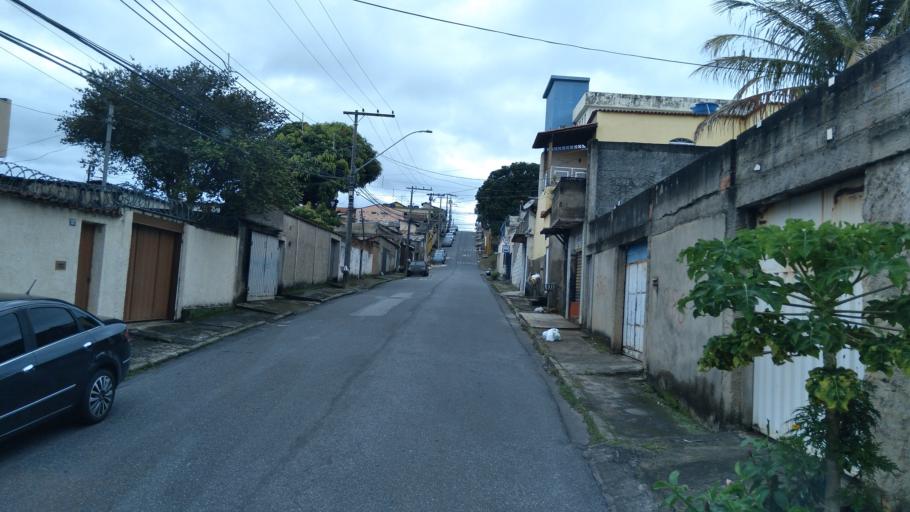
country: BR
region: Minas Gerais
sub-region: Belo Horizonte
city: Belo Horizonte
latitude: -19.9227
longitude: -43.9074
